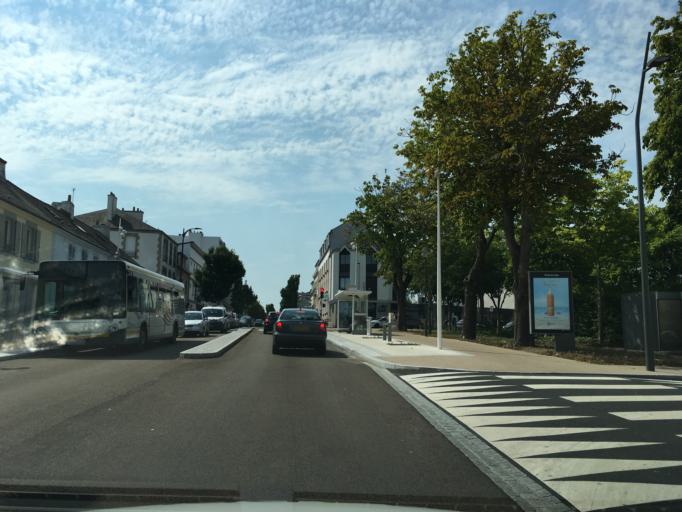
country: FR
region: Brittany
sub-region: Departement du Morbihan
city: Lorient
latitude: 47.7609
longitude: -3.3855
